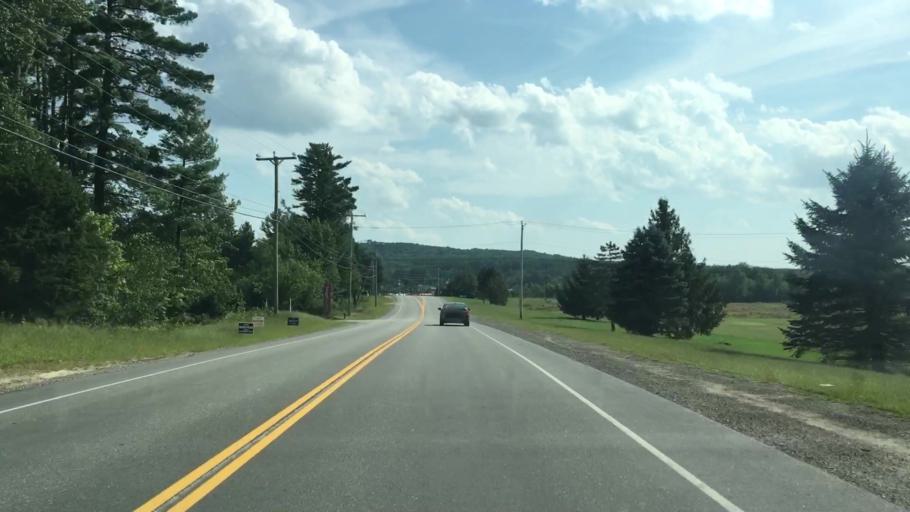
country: US
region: New Hampshire
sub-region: Belknap County
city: Tilton
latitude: 43.4612
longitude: -71.5655
